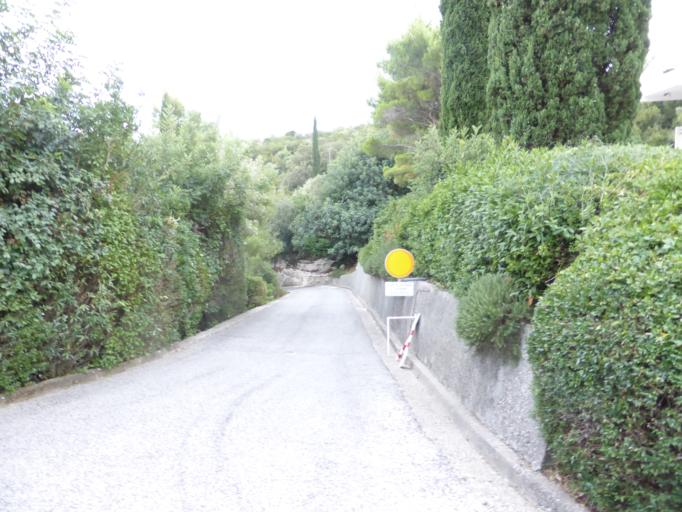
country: HR
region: Dubrovacko-Neretvanska
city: Podgora
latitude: 42.7794
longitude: 17.8683
